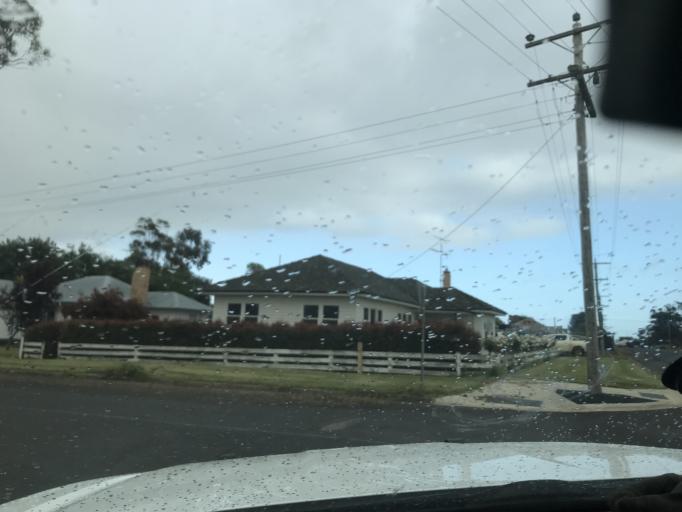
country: AU
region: Victoria
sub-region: Horsham
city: Horsham
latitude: -36.7216
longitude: 141.4763
